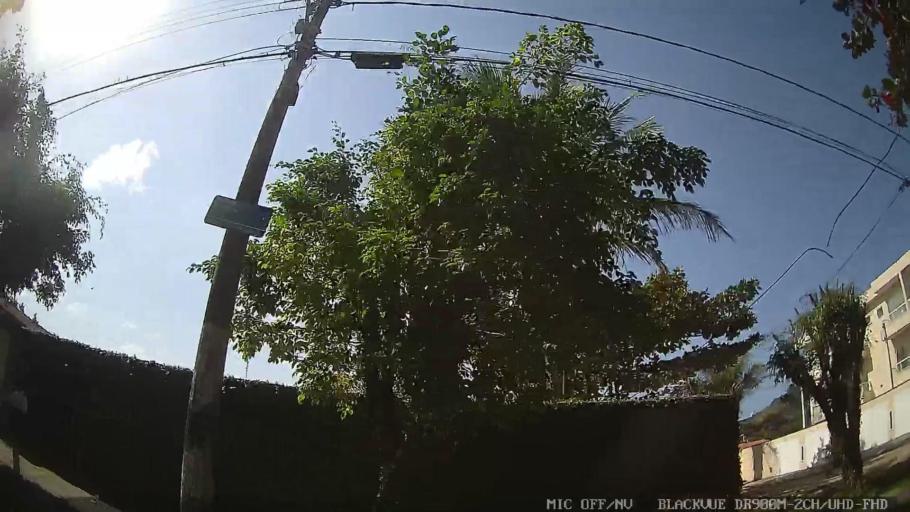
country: BR
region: Sao Paulo
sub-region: Guaruja
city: Guaruja
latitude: -23.9796
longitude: -46.1994
